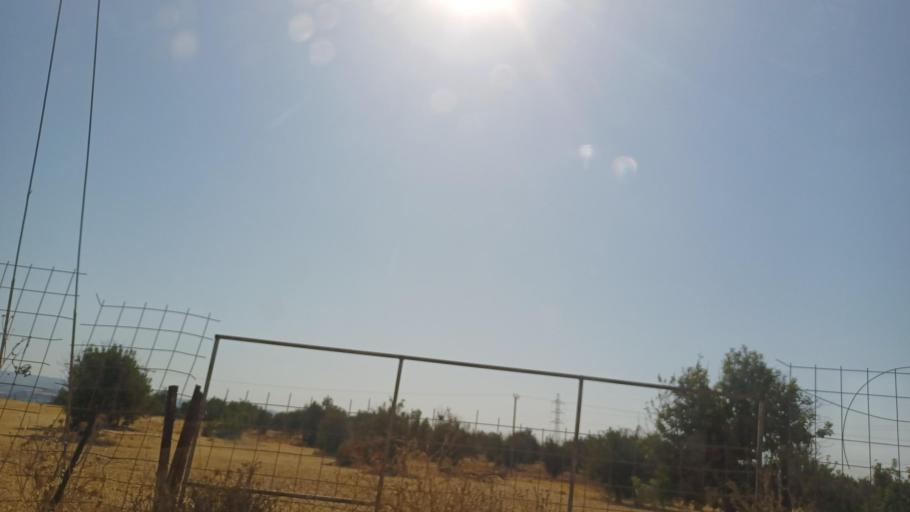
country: CY
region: Limassol
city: Pissouri
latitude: 34.6840
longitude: 32.7402
